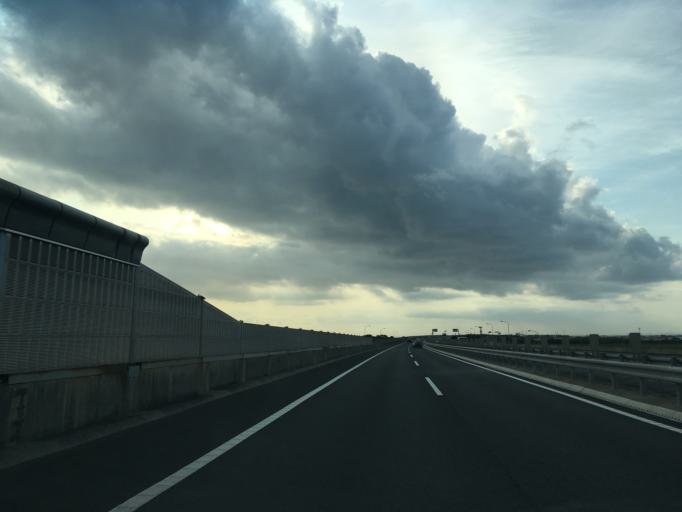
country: JP
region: Chiba
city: Kisarazu
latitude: 35.4194
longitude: 139.9410
